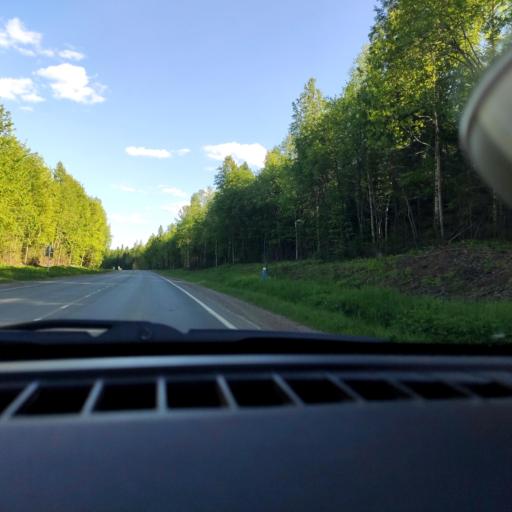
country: RU
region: Perm
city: Perm
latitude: 58.2242
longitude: 56.1647
